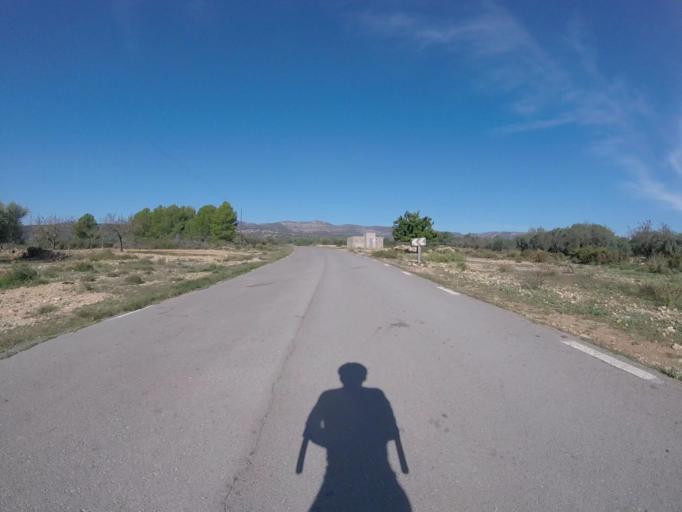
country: ES
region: Valencia
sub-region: Provincia de Castello
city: Sarratella
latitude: 40.2679
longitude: 0.0639
